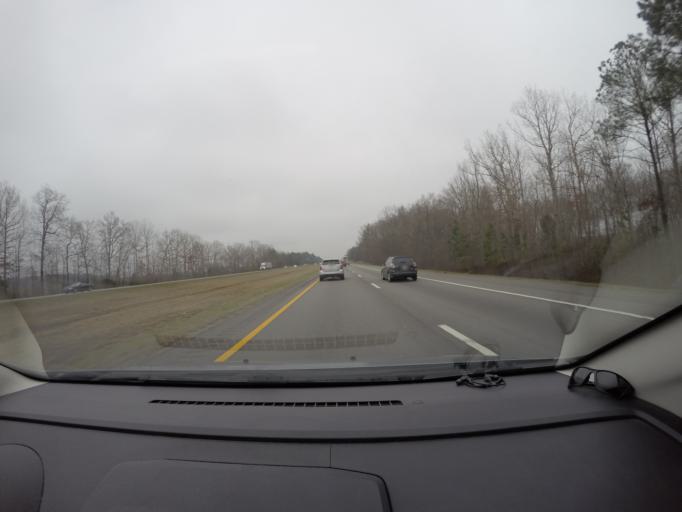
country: US
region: Tennessee
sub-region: Coffee County
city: New Union
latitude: 35.5224
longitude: -86.1329
